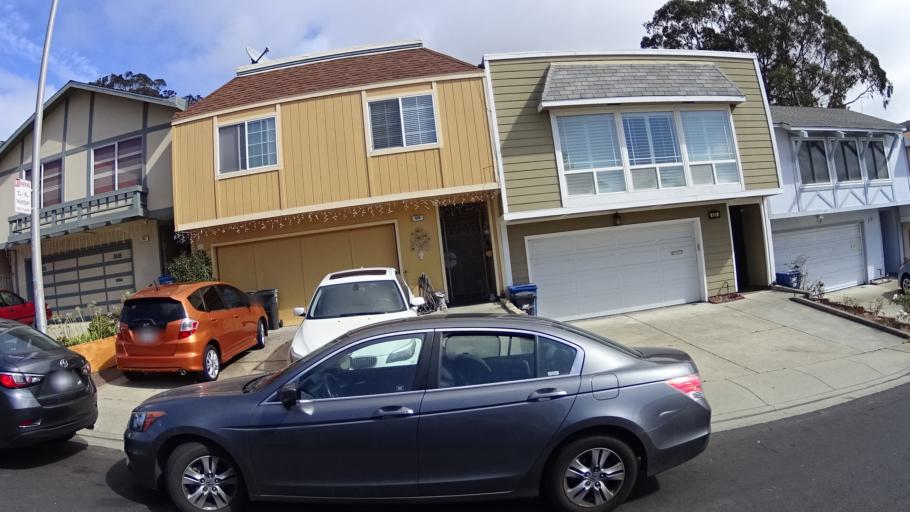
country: US
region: California
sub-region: San Mateo County
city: Daly City
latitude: 37.6955
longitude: -122.4572
